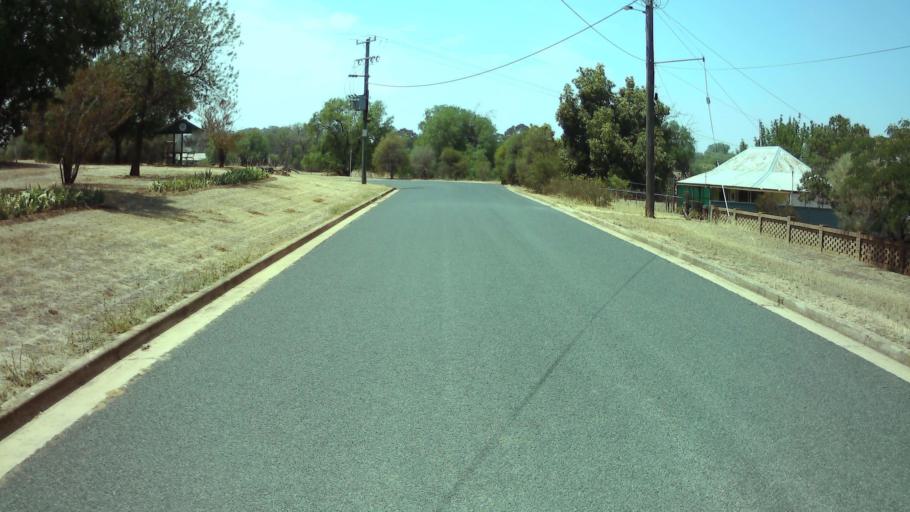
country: AU
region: New South Wales
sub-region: Weddin
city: Grenfell
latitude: -33.8973
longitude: 148.1675
